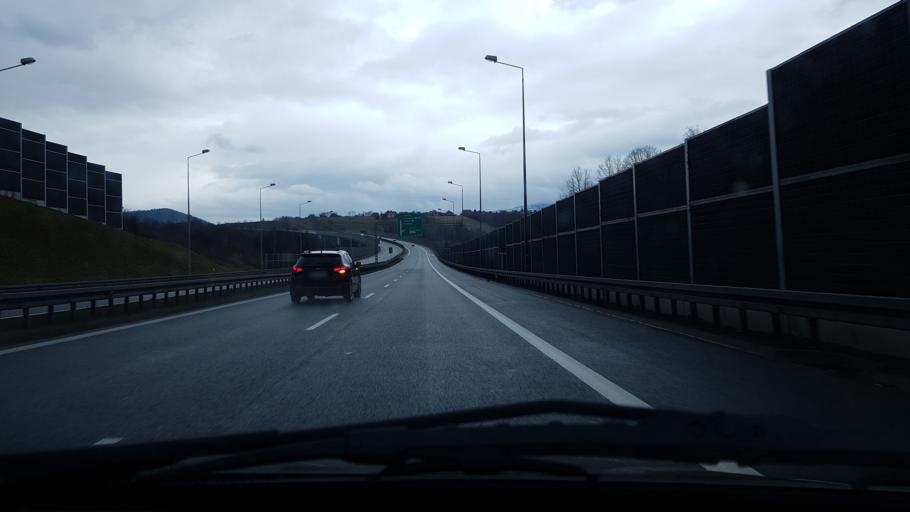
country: PL
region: Silesian Voivodeship
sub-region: Bielsko-Biala
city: Bielsko-Biala
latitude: 49.8347
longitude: 19.0858
